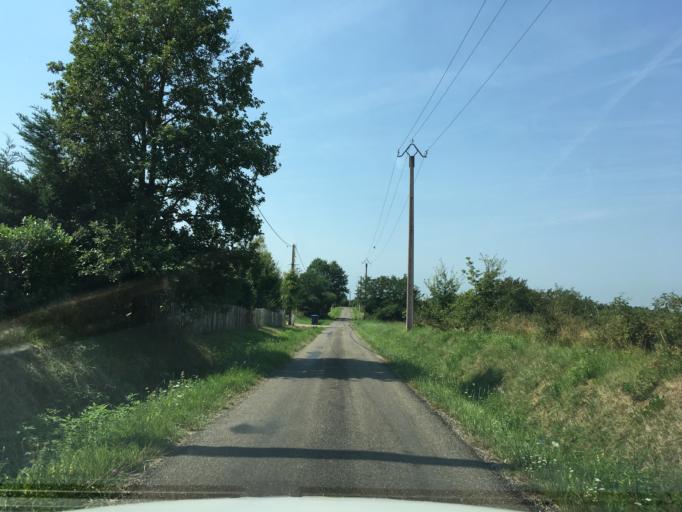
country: FR
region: Midi-Pyrenees
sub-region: Departement du Tarn-et-Garonne
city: Saint-Nauphary
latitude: 44.0104
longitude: 1.4195
